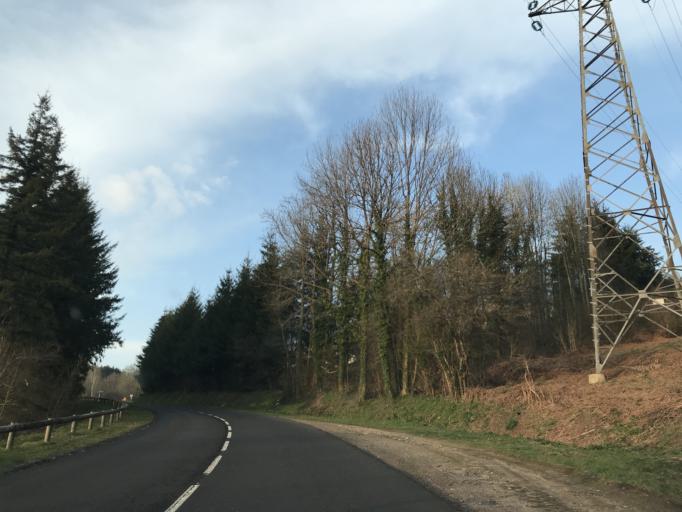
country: FR
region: Auvergne
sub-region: Departement du Puy-de-Dome
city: La Monnerie-le-Montel
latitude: 45.8754
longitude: 3.5907
